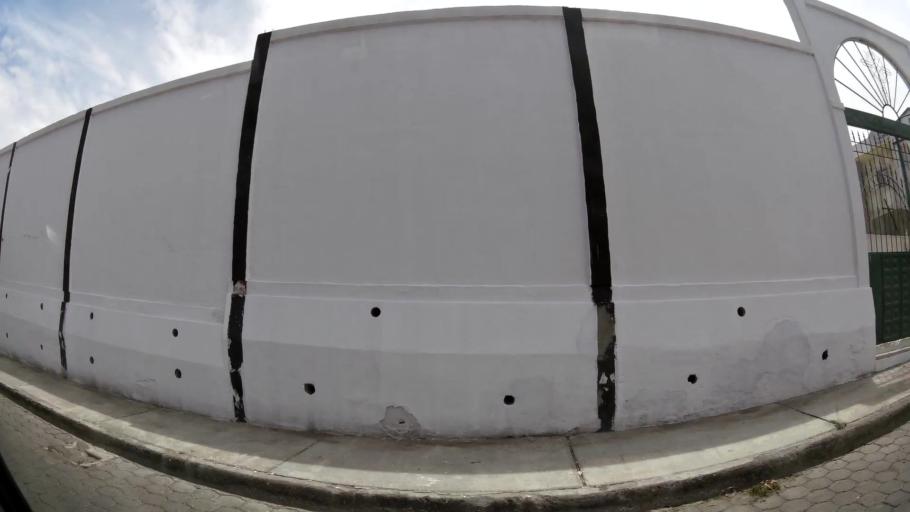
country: EC
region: Cotopaxi
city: San Miguel de Salcedo
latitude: -1.0432
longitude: -78.5836
